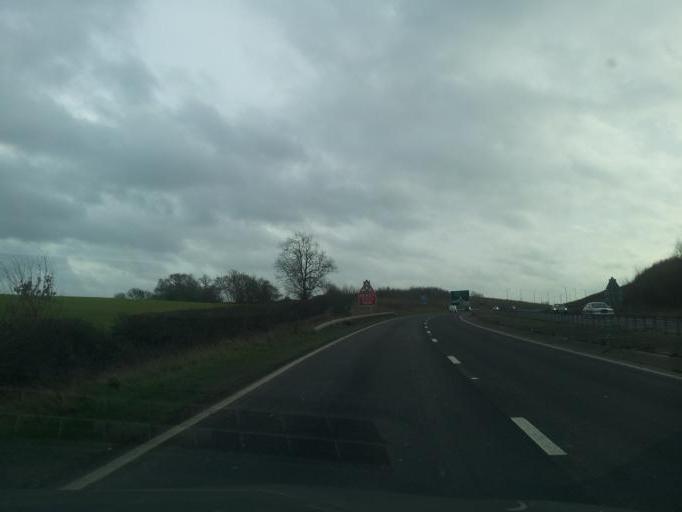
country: GB
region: England
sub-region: Central Bedfordshire
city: Leighton Buzzard
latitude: 51.9316
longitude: -0.6961
